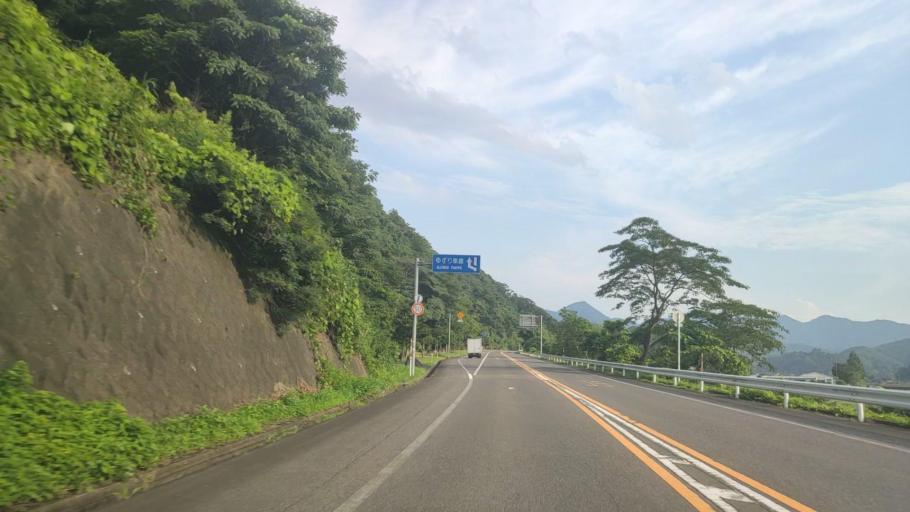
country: JP
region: Tottori
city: Kurayoshi
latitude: 35.3598
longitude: 133.7517
